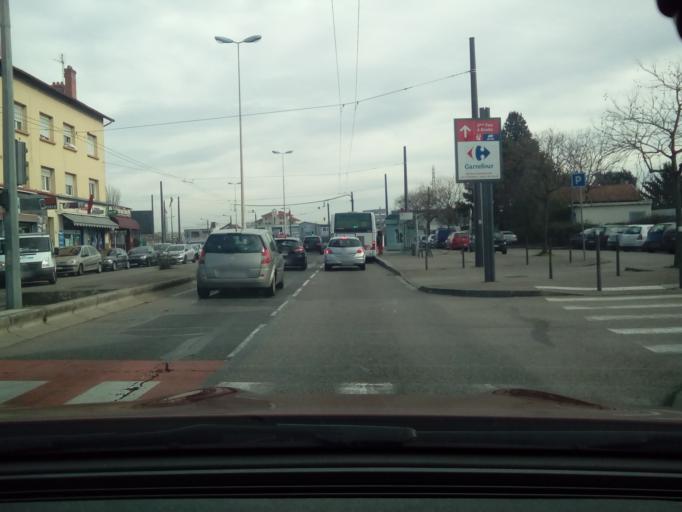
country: FR
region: Rhone-Alpes
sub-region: Departement du Rhone
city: Vaulx-en-Velin
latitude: 45.7719
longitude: 4.9107
